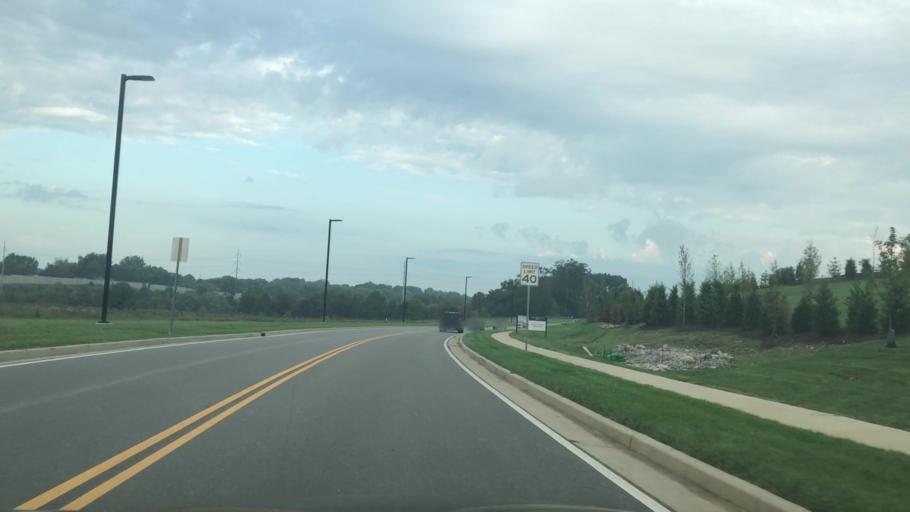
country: US
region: Tennessee
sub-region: Williamson County
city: Franklin
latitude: 35.8910
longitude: -86.8238
